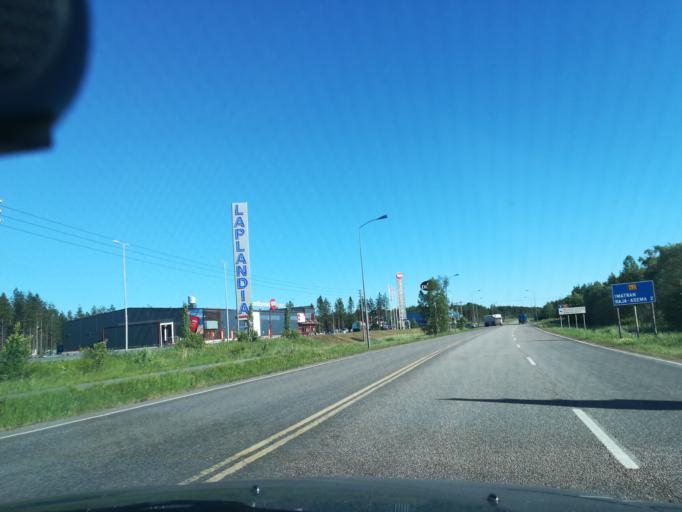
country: FI
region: South Karelia
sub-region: Imatra
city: Imatra
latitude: 61.1507
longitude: 28.8086
